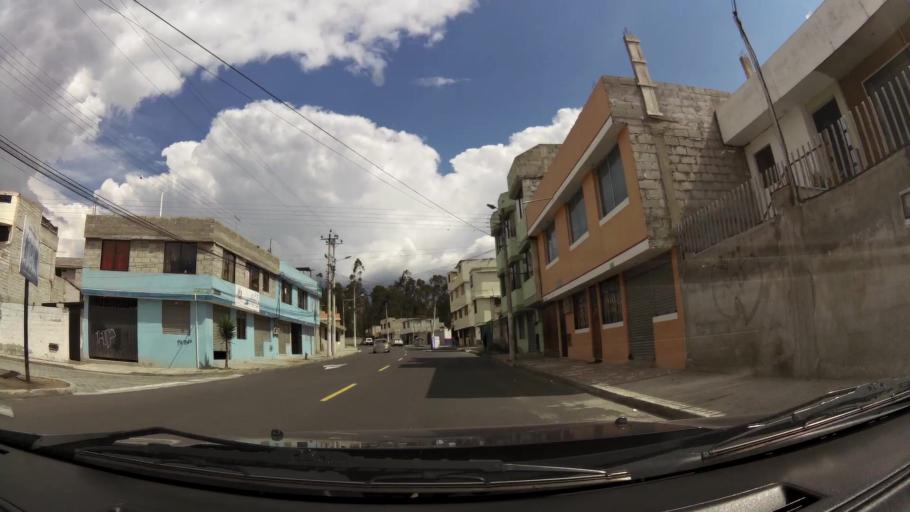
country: EC
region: Pichincha
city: Quito
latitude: -0.0998
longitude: -78.4552
